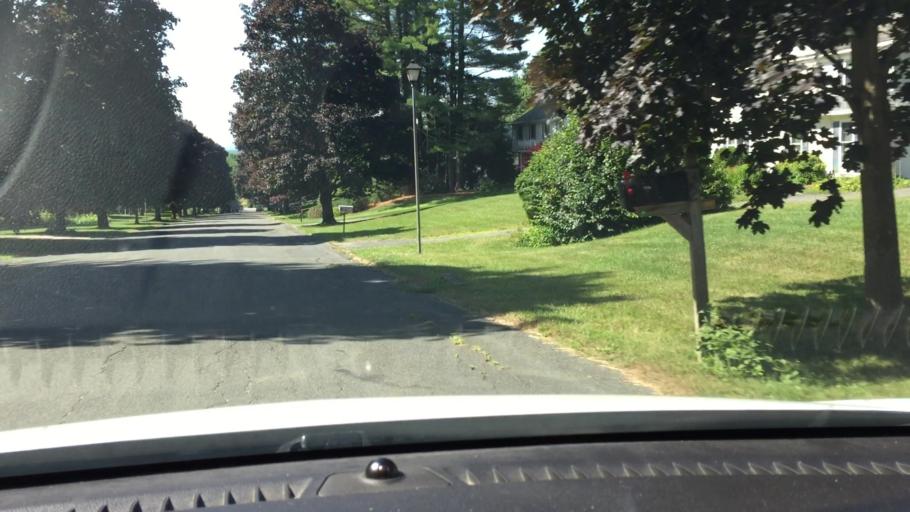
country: US
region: Massachusetts
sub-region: Berkshire County
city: Pittsfield
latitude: 42.4345
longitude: -73.2354
